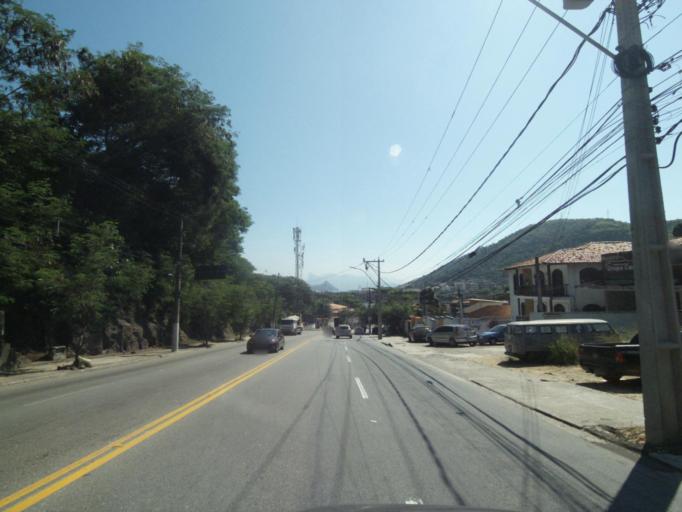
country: BR
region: Rio de Janeiro
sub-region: Niteroi
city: Niteroi
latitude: -22.9121
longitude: -43.0758
